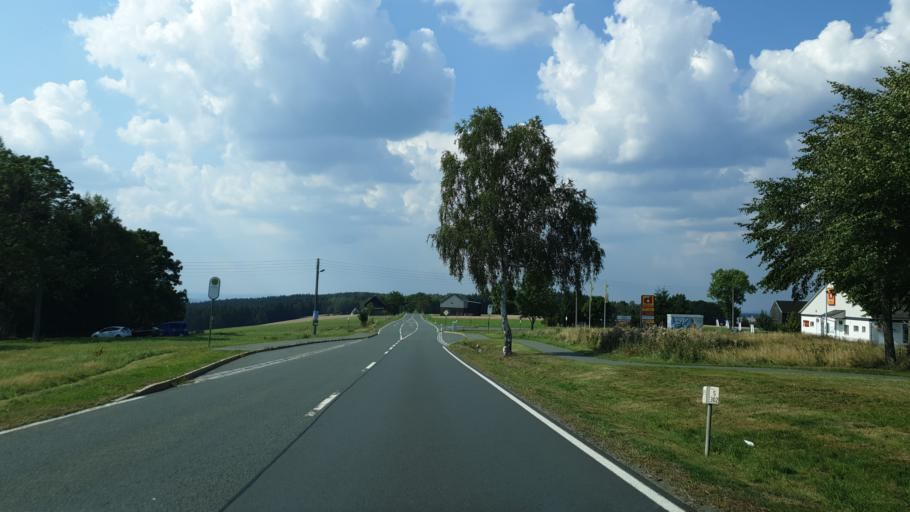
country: DE
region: Saxony
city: Pohl
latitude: 50.3966
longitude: 12.3282
